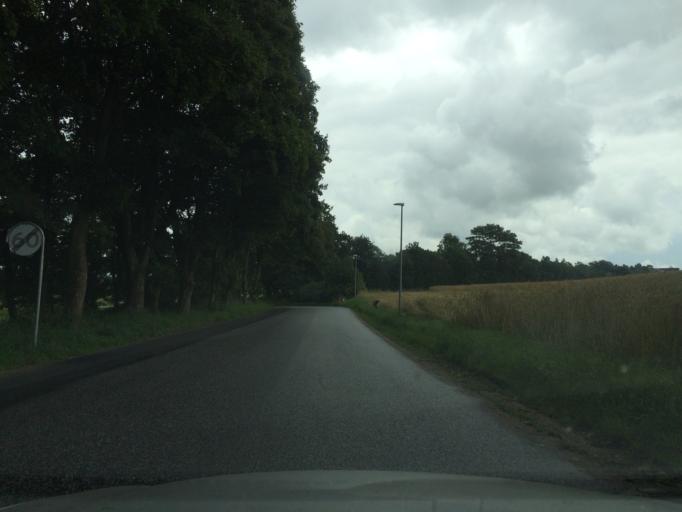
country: DK
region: Central Jutland
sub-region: Skanderborg Kommune
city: Ry
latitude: 56.2160
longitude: 9.7416
